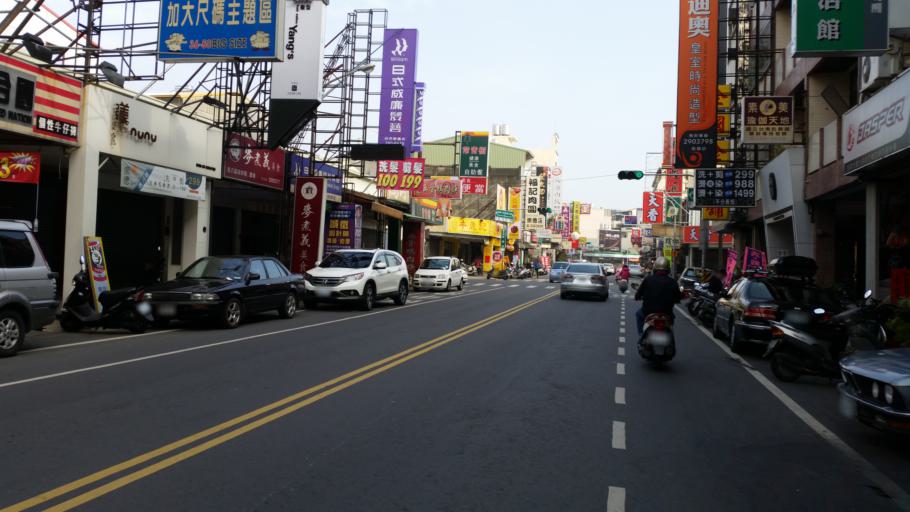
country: TW
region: Taiwan
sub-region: Tainan
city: Tainan
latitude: 22.9750
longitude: 120.2261
